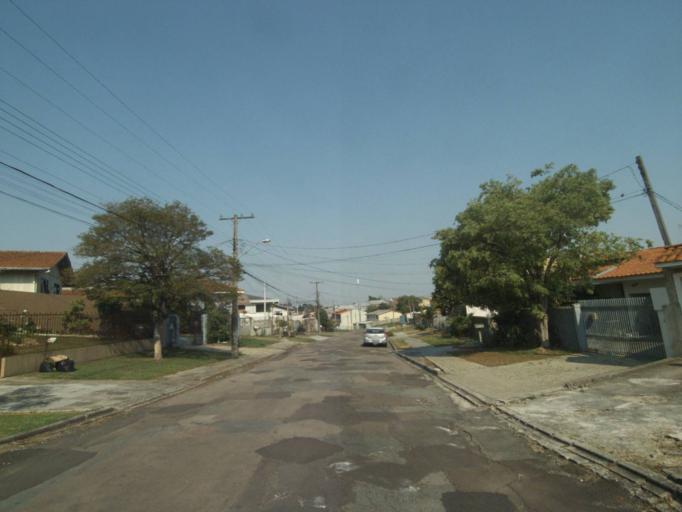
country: BR
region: Parana
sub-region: Sao Jose Dos Pinhais
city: Sao Jose dos Pinhais
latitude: -25.5053
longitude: -49.2726
